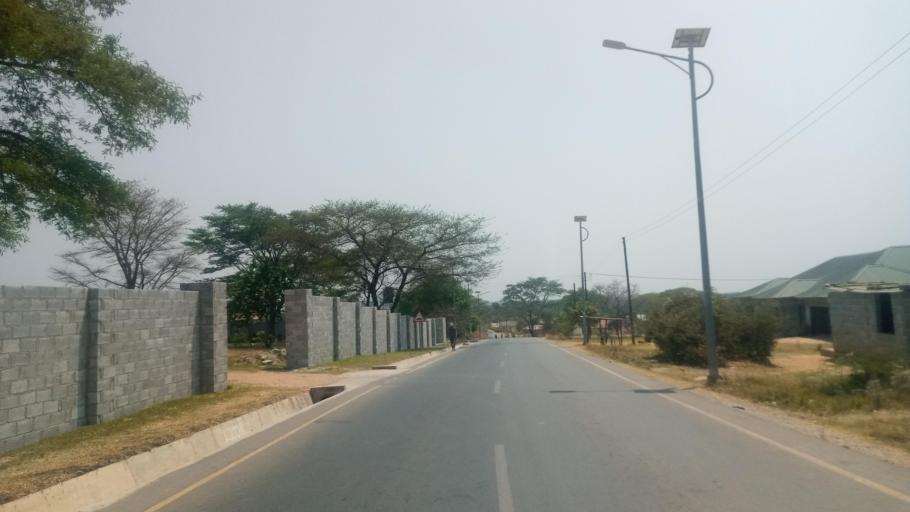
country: ZM
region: Lusaka
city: Lusaka
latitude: -15.4524
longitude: 28.4409
